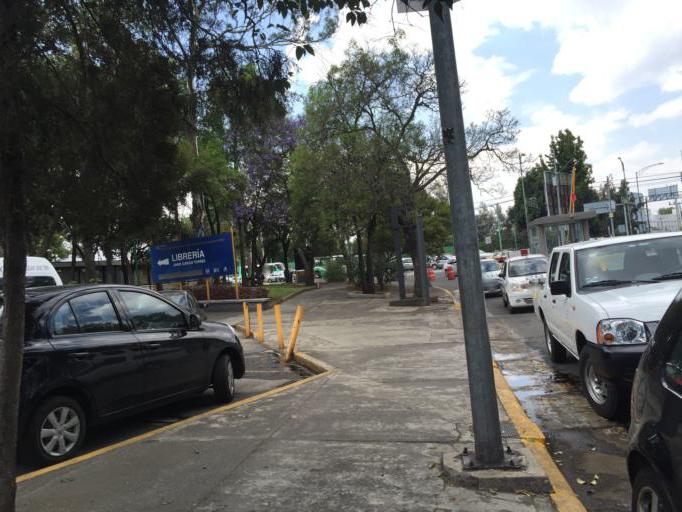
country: MX
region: Mexico City
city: Magdalena Contreras
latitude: 19.3363
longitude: -99.1862
